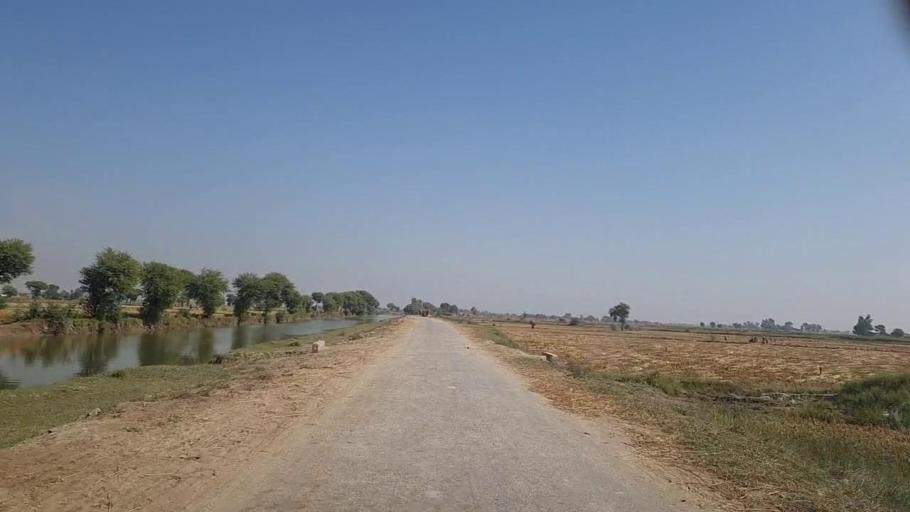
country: PK
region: Sindh
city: Thul
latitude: 28.2523
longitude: 68.8162
